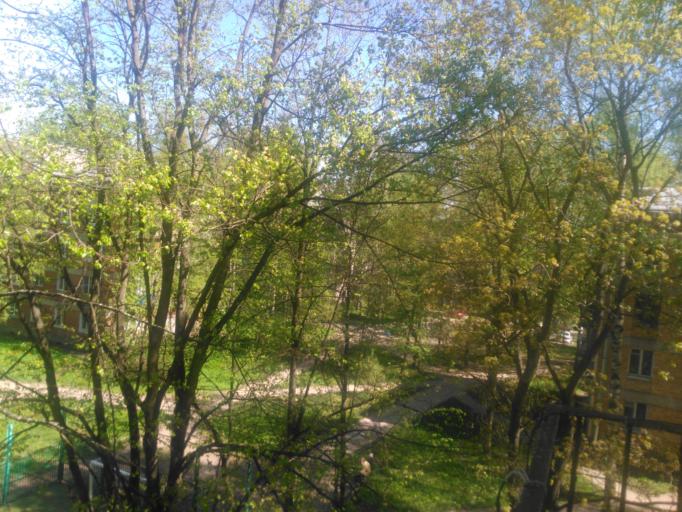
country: RU
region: St.-Petersburg
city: Pushkin
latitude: 59.7263
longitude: 30.4253
